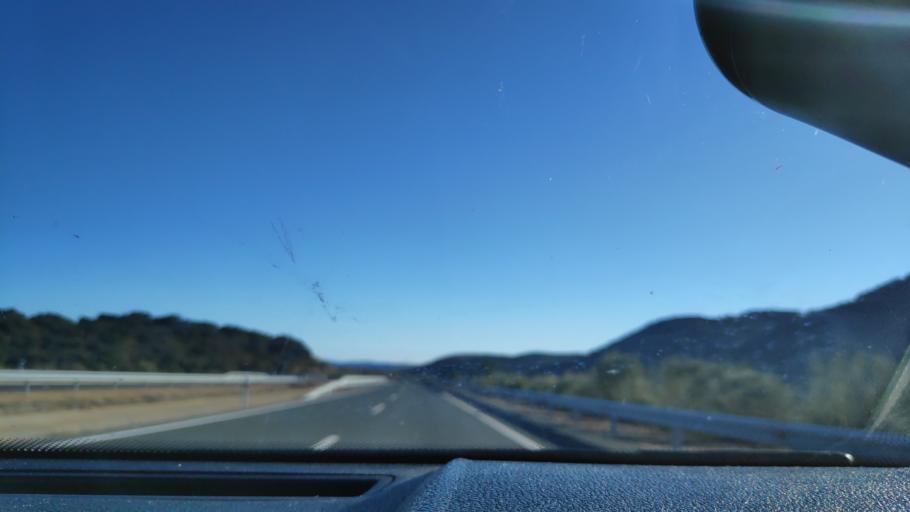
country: ES
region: Extremadura
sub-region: Provincia de Badajoz
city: Monesterio
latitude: 38.0556
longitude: -6.2394
